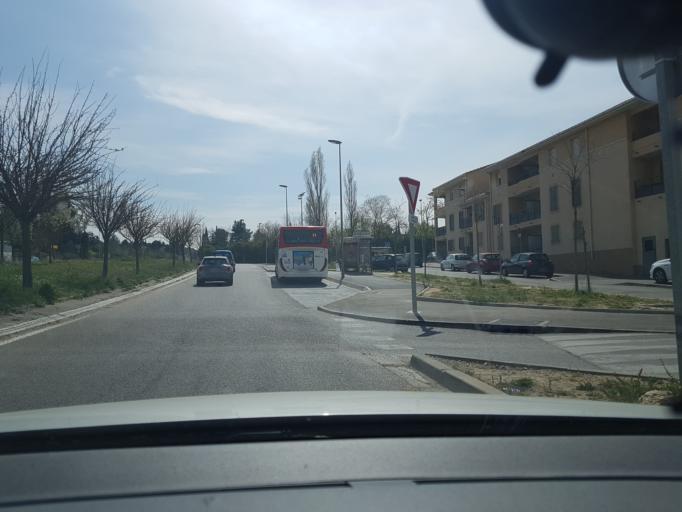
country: FR
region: Provence-Alpes-Cote d'Azur
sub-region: Departement des Bouches-du-Rhone
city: Bouc-Bel-Air
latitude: 43.4808
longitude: 5.4149
